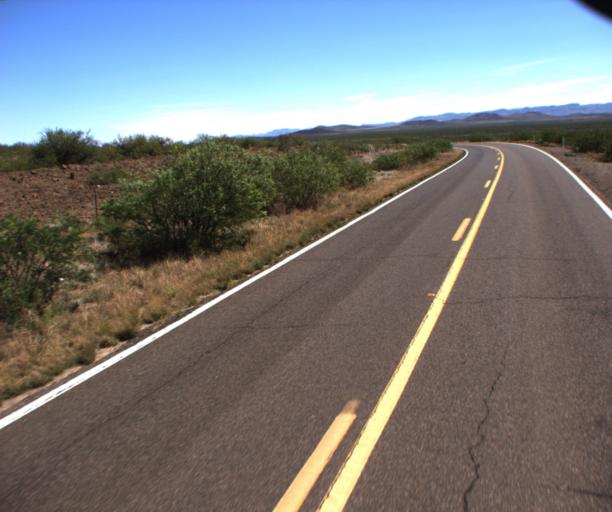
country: US
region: Arizona
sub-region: Cochise County
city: Douglas
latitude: 31.4606
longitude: -109.3685
